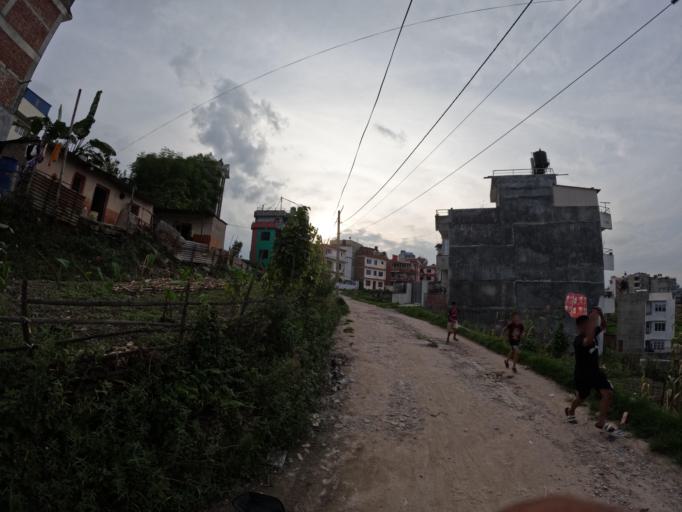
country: NP
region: Central Region
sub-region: Bagmati Zone
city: Bhaktapur
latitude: 27.6832
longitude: 85.3928
